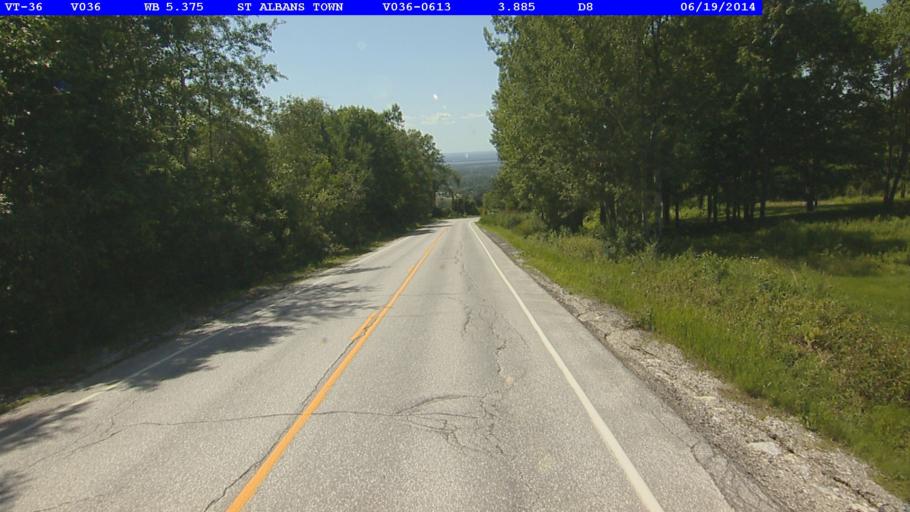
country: US
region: Vermont
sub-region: Franklin County
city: Saint Albans
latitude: 44.7979
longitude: -73.0553
